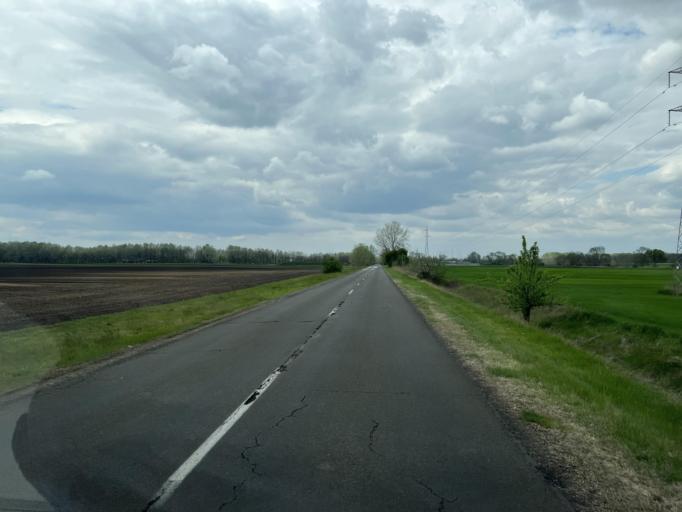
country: HU
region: Pest
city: Ujhartyan
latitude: 47.2011
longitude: 19.4045
